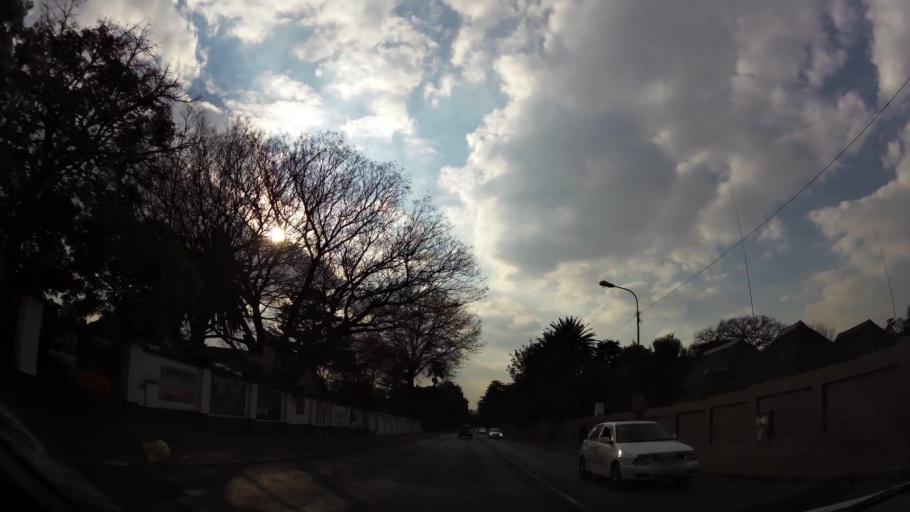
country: ZA
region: Gauteng
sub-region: Ekurhuleni Metropolitan Municipality
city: Germiston
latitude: -26.2373
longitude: 28.1749
